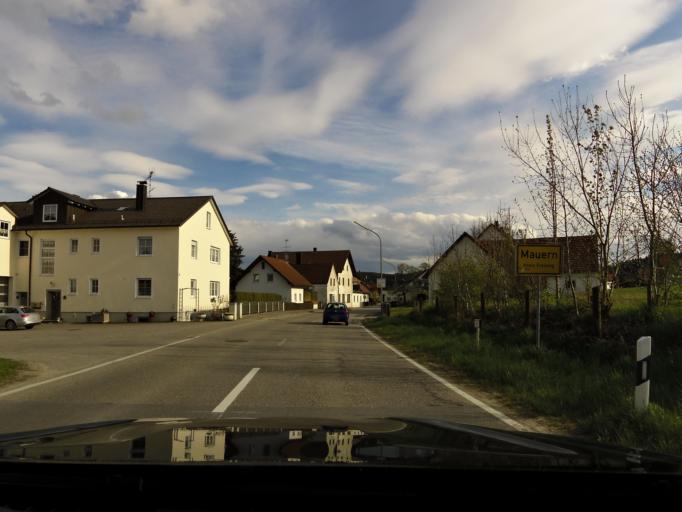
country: DE
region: Bavaria
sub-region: Upper Bavaria
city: Mauern
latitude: 48.5193
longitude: 11.8955
